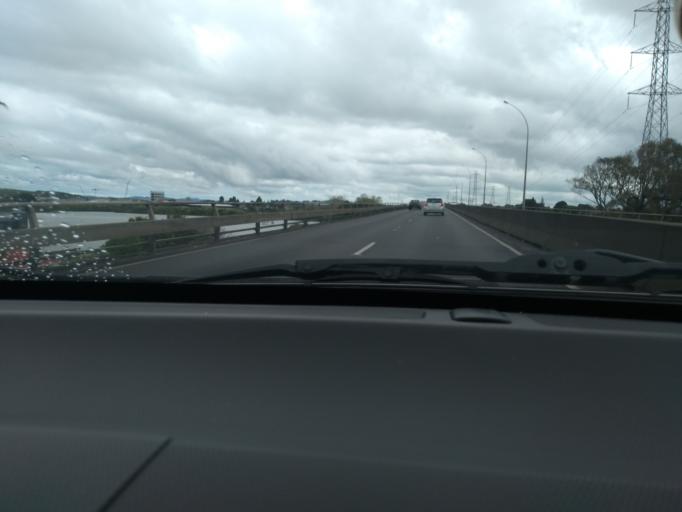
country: NZ
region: Auckland
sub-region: Auckland
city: Tamaki
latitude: -36.9134
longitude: 174.8614
